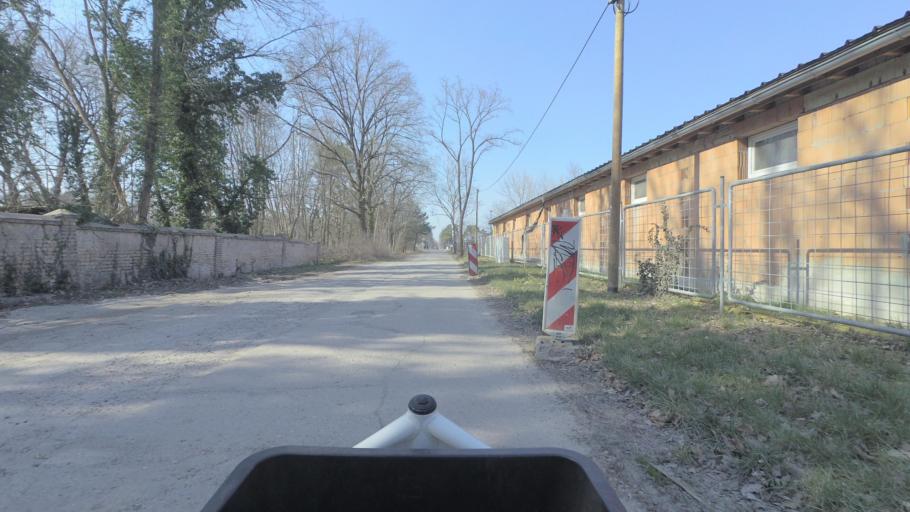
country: DE
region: Brandenburg
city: Sperenberg
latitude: 52.1615
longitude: 13.3735
